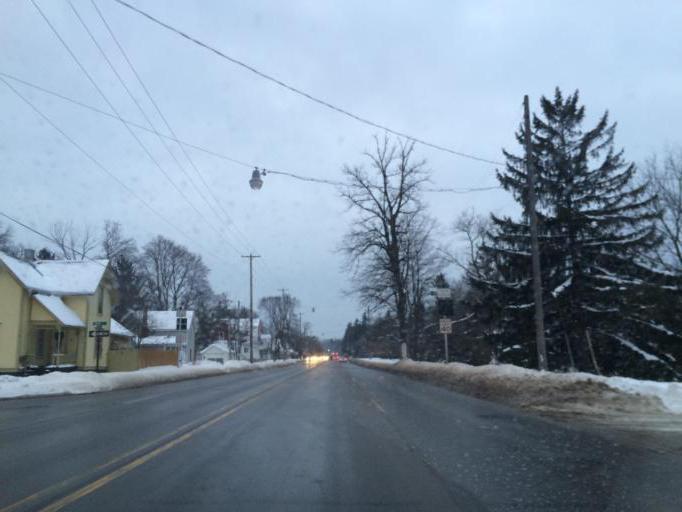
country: US
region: Michigan
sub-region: Grand Traverse County
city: Traverse City
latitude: 44.7595
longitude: -85.6347
